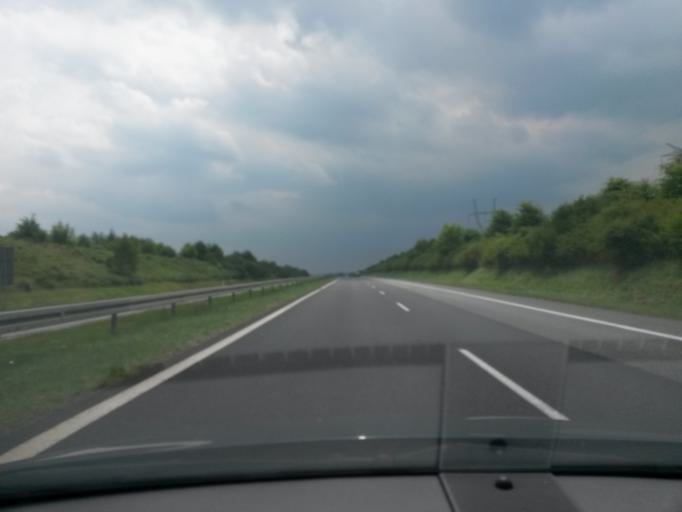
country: PL
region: Lodz Voivodeship
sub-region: Powiat radomszczanski
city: Radomsko
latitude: 51.0913
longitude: 19.3770
